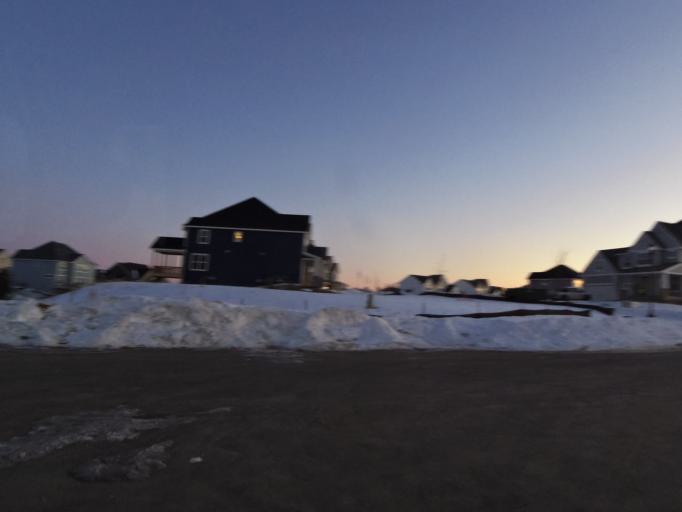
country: US
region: Minnesota
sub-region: Washington County
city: Lake Elmo
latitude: 45.0100
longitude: -92.8789
